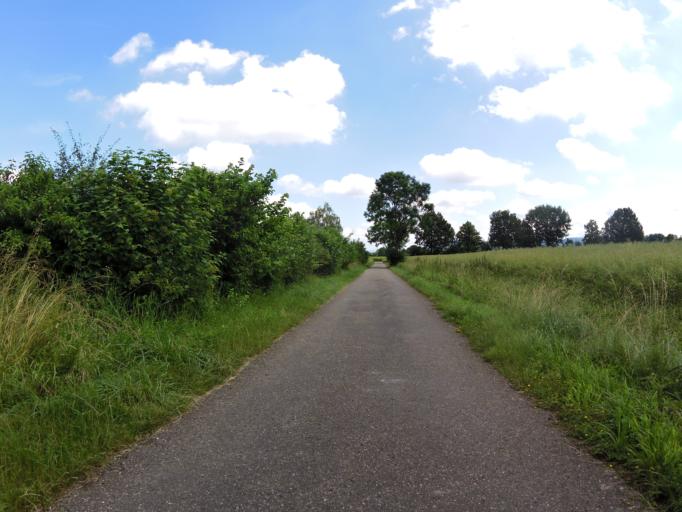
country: DE
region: Baden-Wuerttemberg
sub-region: Freiburg Region
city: Kippenheim
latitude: 48.3350
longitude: 7.8131
